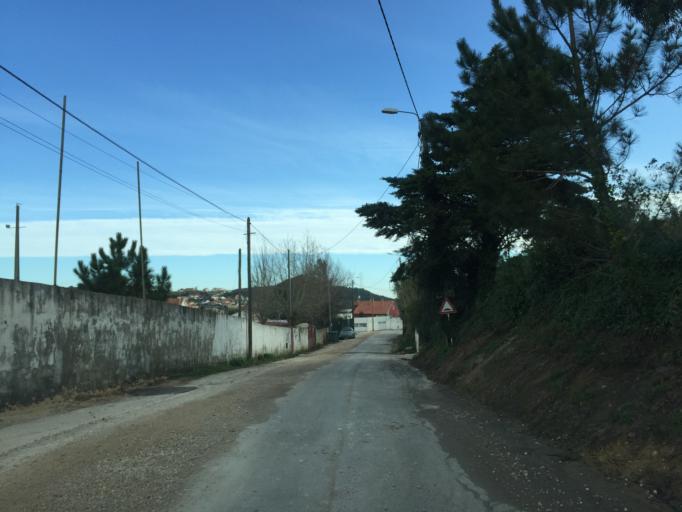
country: PT
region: Lisbon
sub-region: Odivelas
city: Canecas
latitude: 38.8235
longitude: -9.2450
